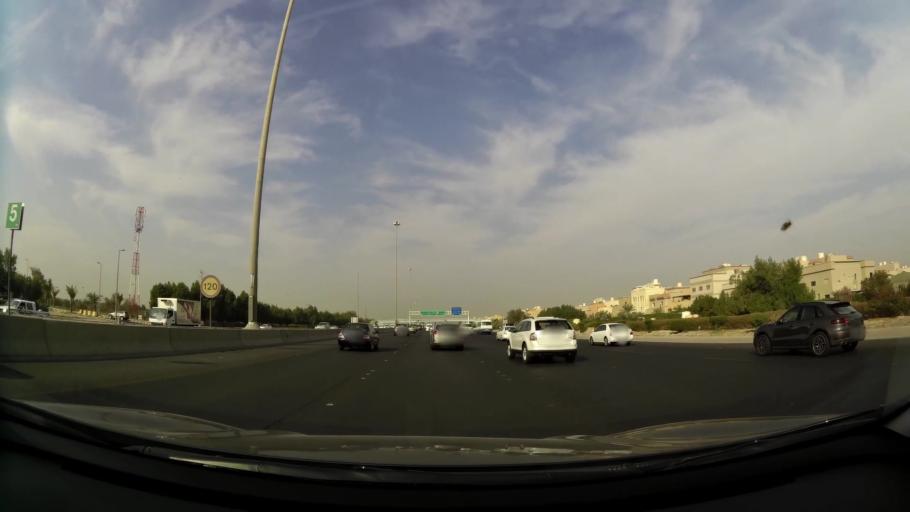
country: KW
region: Mubarak al Kabir
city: Sabah as Salim
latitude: 29.2650
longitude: 48.0331
